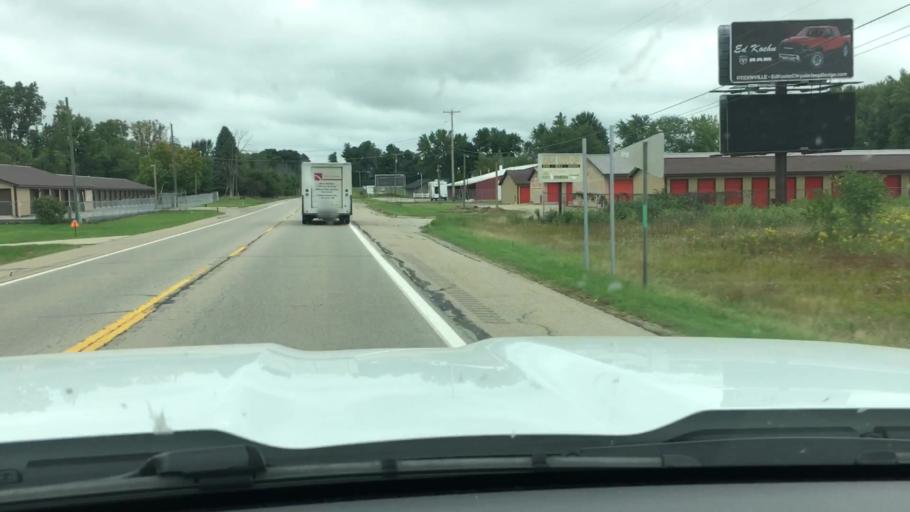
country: US
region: Michigan
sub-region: Ionia County
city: Ionia
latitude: 43.0306
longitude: -85.0766
